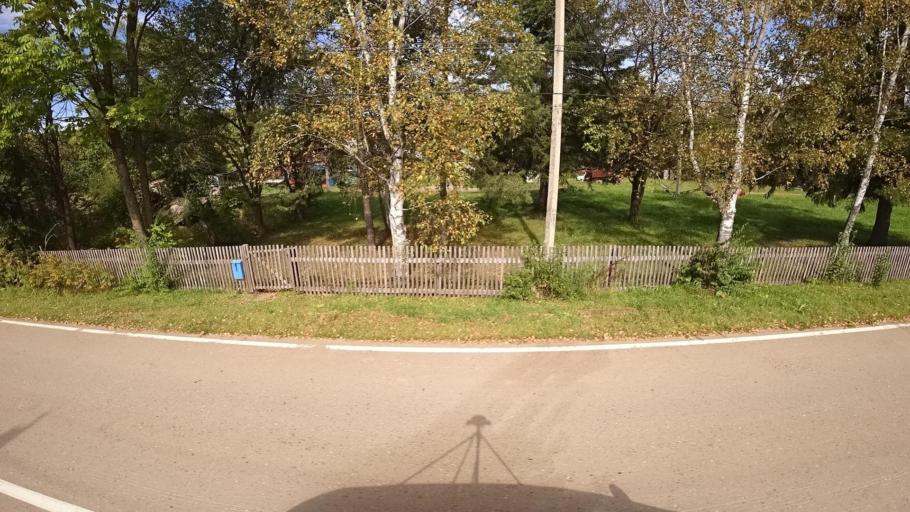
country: RU
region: Primorskiy
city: Yakovlevka
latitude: 44.3970
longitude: 133.6019
